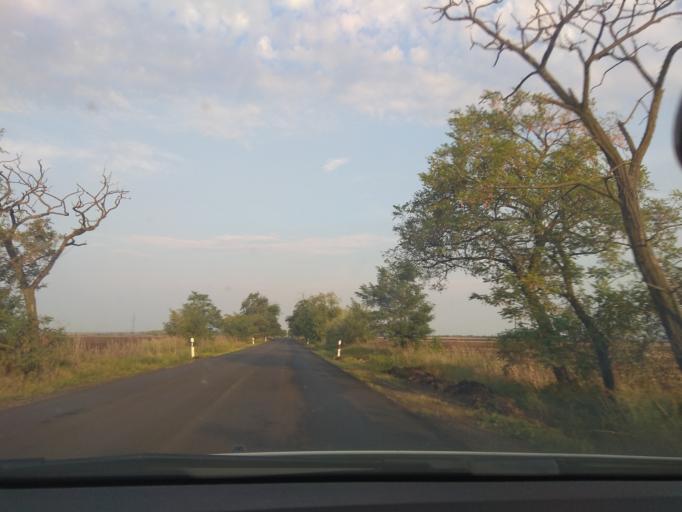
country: HU
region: Borsod-Abauj-Zemplen
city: Mezokovesd
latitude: 47.8135
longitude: 20.5287
